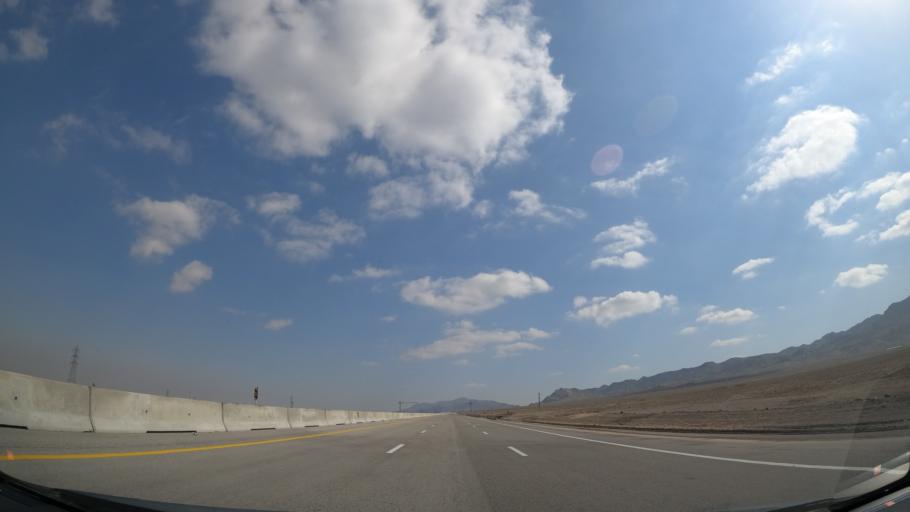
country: IR
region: Alborz
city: Eshtehard
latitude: 35.7151
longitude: 50.5824
